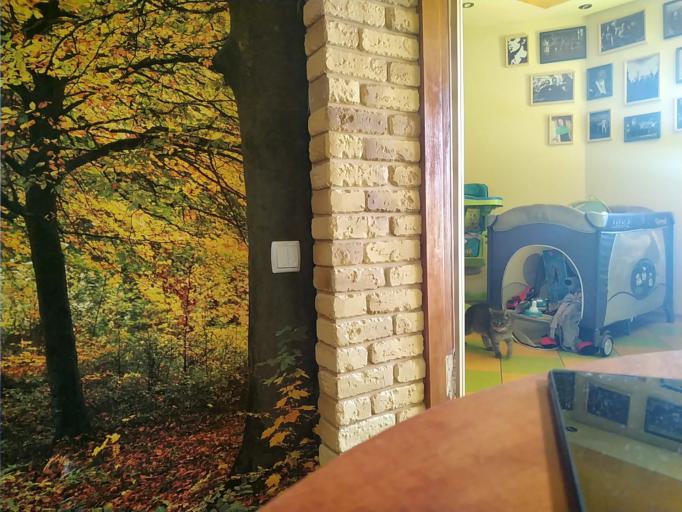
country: RU
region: Tverskaya
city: Vyshniy Volochek
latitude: 57.5660
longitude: 34.5725
